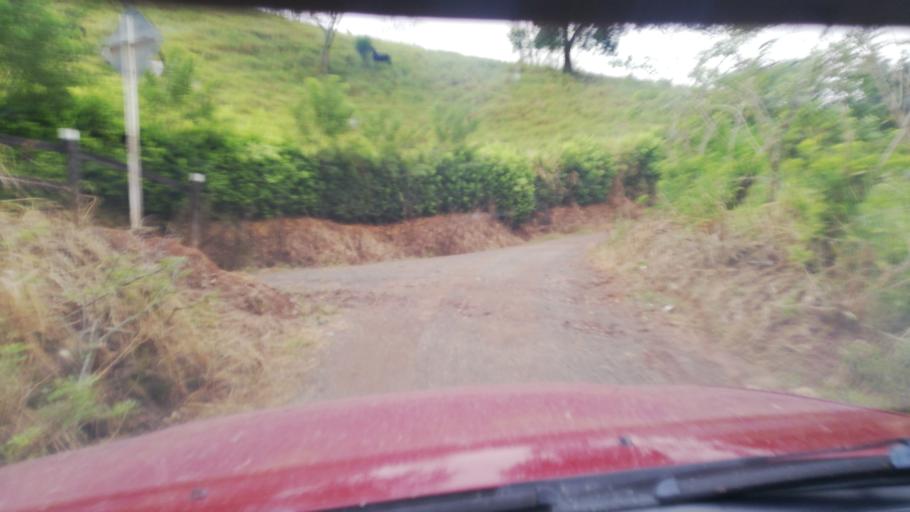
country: CO
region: Risaralda
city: Balboa
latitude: 4.8869
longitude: -75.9507
